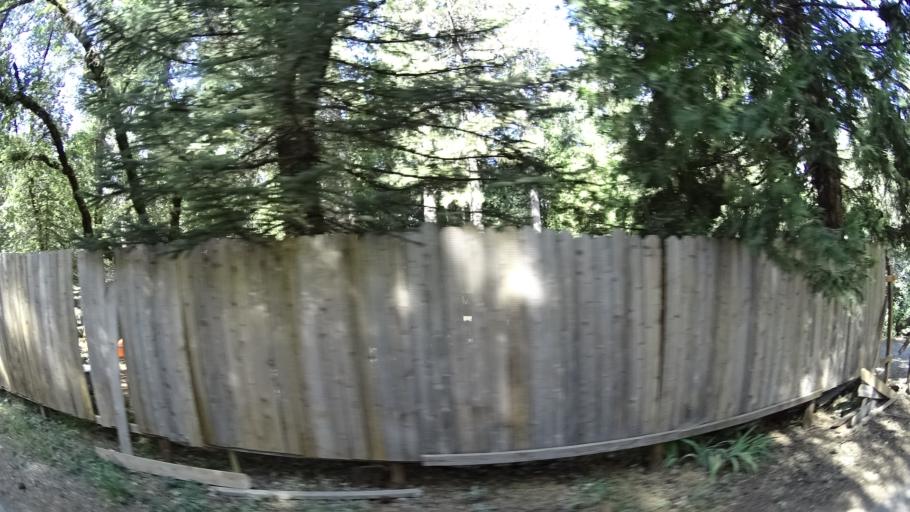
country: US
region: California
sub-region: Amador County
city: Pioneer
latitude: 38.3990
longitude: -120.5177
